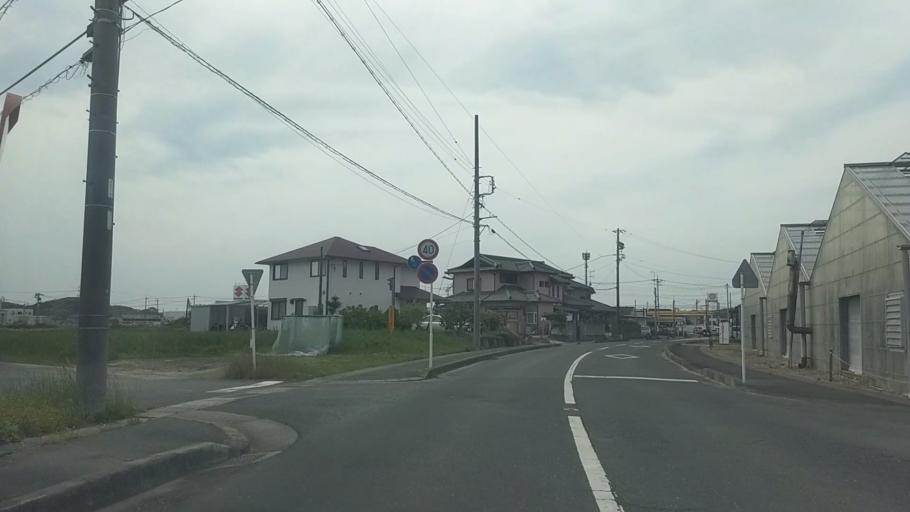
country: JP
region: Shizuoka
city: Kosai-shi
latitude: 34.7300
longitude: 137.5251
